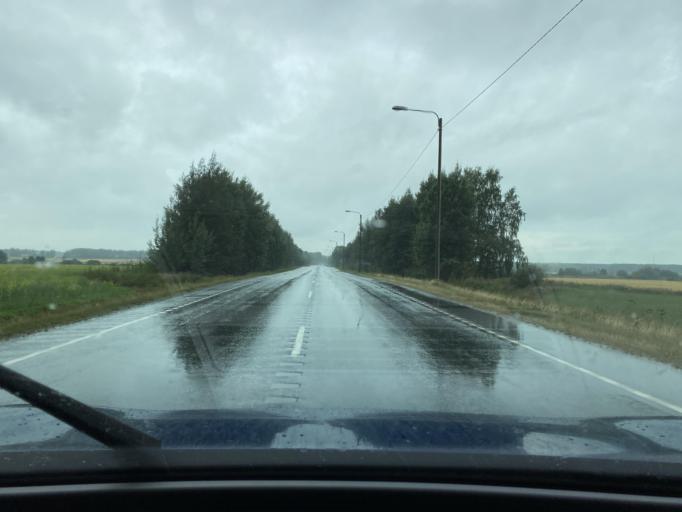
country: FI
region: Southern Ostrobothnia
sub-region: Seinaejoki
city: Ylihaermae
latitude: 63.1386
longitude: 22.8630
